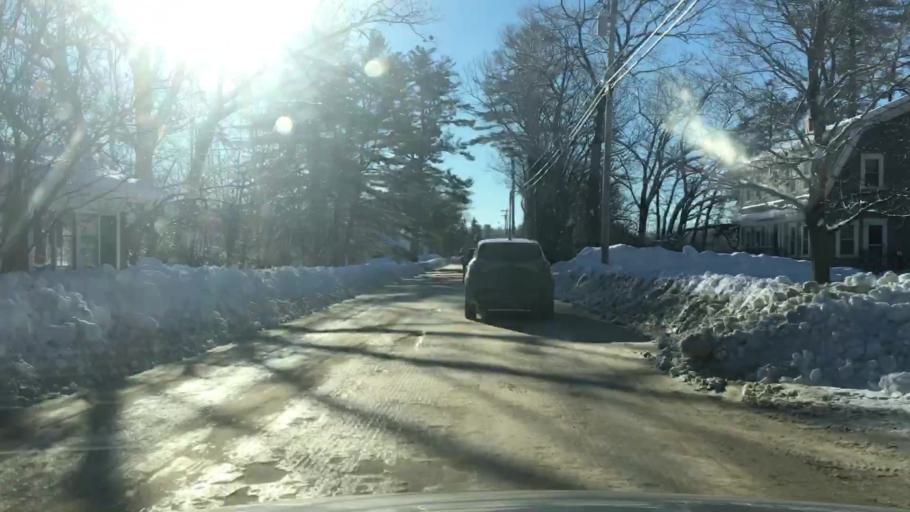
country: US
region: Maine
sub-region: Oxford County
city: West Paris
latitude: 44.3852
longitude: -70.6439
